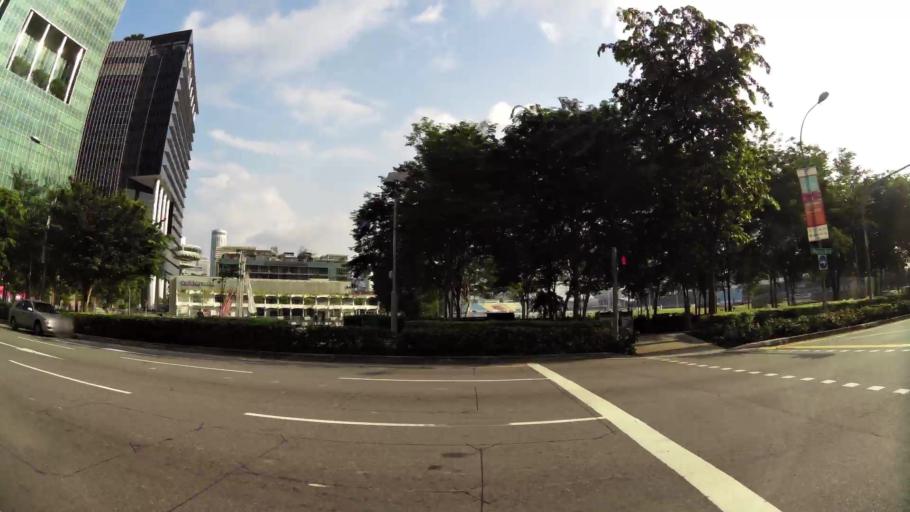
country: SG
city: Singapore
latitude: 1.2813
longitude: 103.8535
